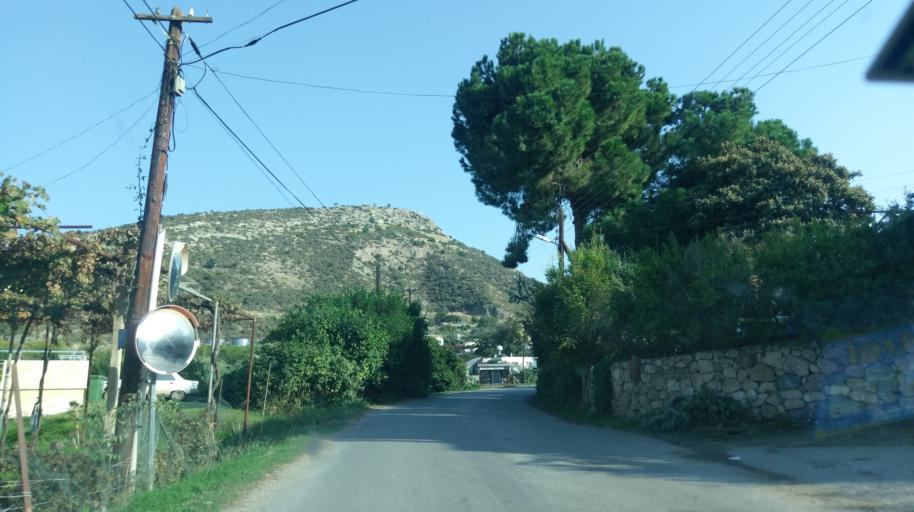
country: CY
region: Lefkosia
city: Kato Pyrgos
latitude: 35.1677
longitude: 32.7443
